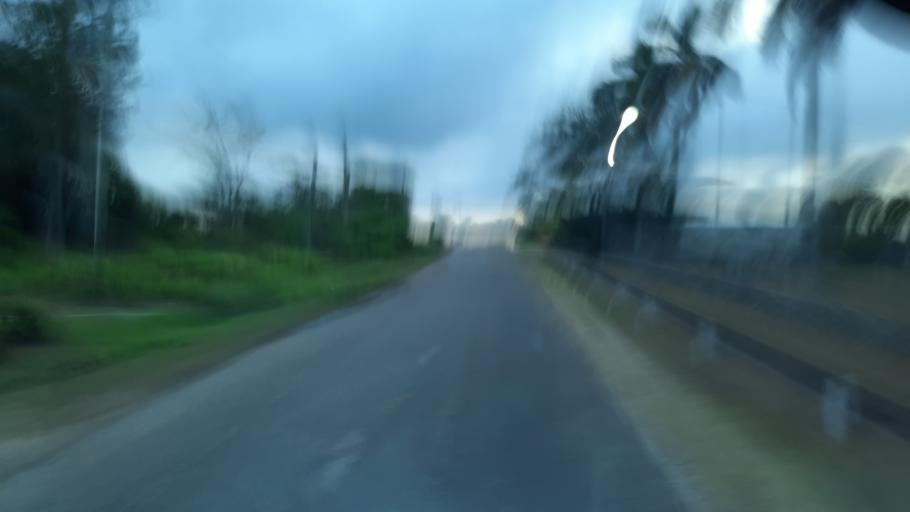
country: BZ
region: Belize
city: Belize City
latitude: 17.5435
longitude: -88.2985
